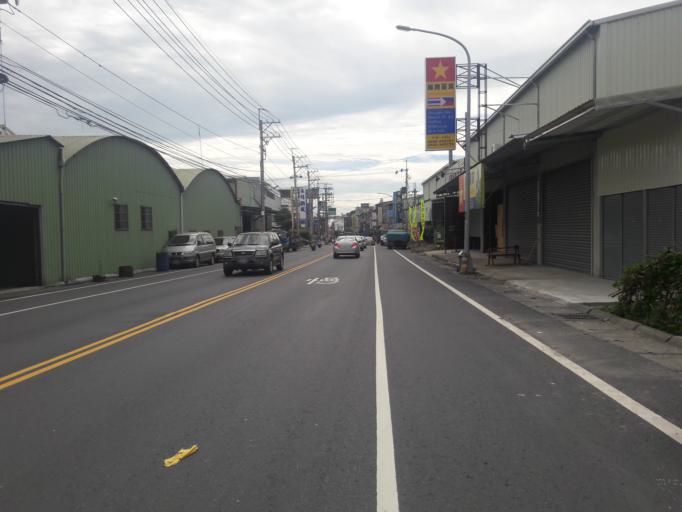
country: TW
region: Taiwan
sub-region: Taichung City
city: Taichung
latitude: 24.0950
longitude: 120.7080
